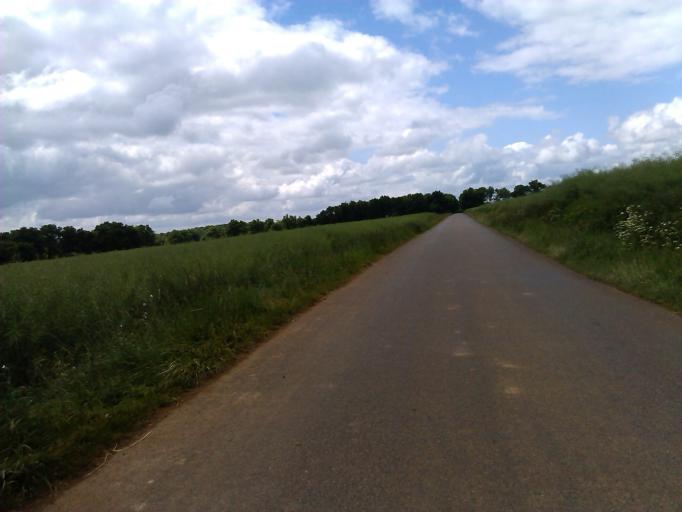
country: FR
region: Poitou-Charentes
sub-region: Departement de la Charente
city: Champagne-Mouton
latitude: 46.0651
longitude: 0.4854
